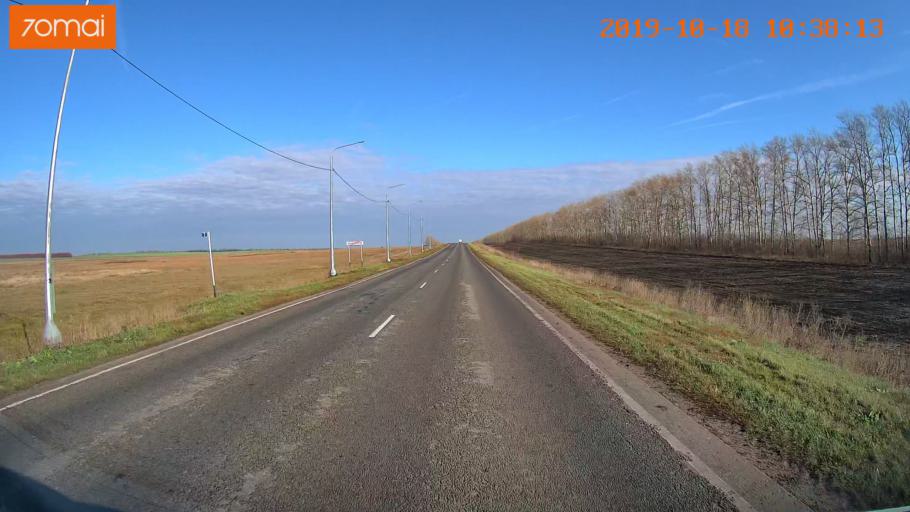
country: RU
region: Tula
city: Kurkino
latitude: 53.5699
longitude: 38.6389
